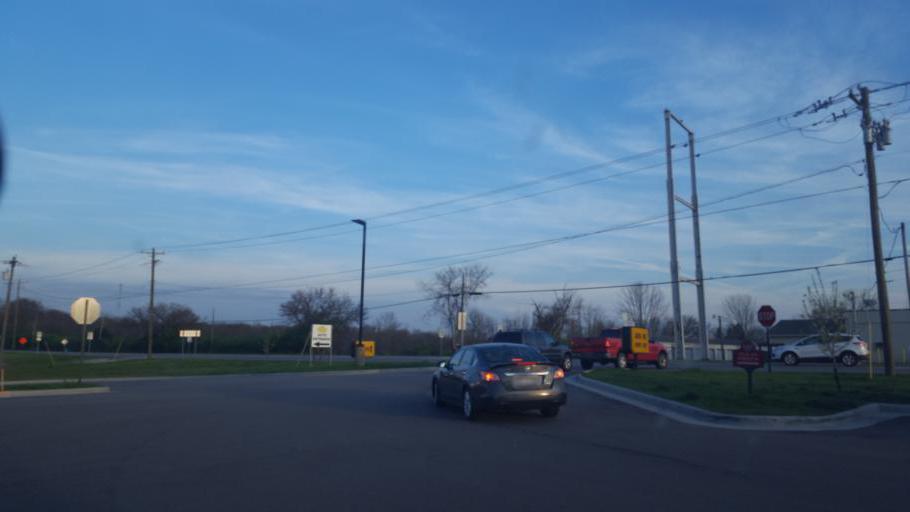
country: US
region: Ohio
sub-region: Warren County
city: Lebanon
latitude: 39.4111
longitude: -84.1500
